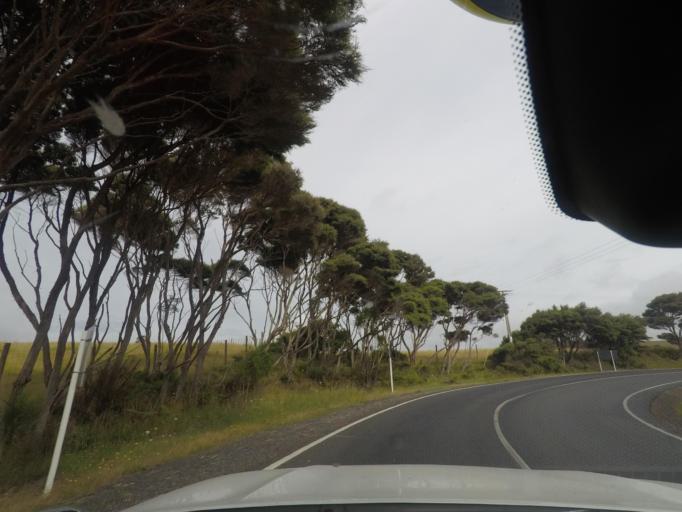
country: NZ
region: Auckland
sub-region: Auckland
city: Parakai
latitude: -36.4939
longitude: 174.2468
